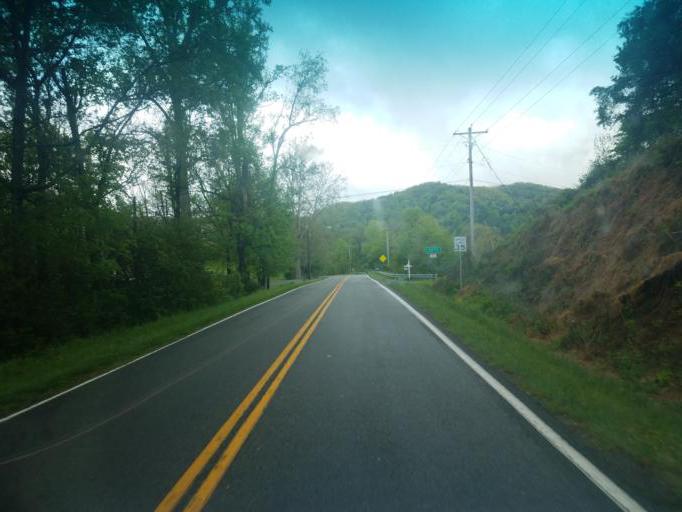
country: US
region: Virginia
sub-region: Washington County
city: Emory
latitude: 36.6398
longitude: -81.7908
